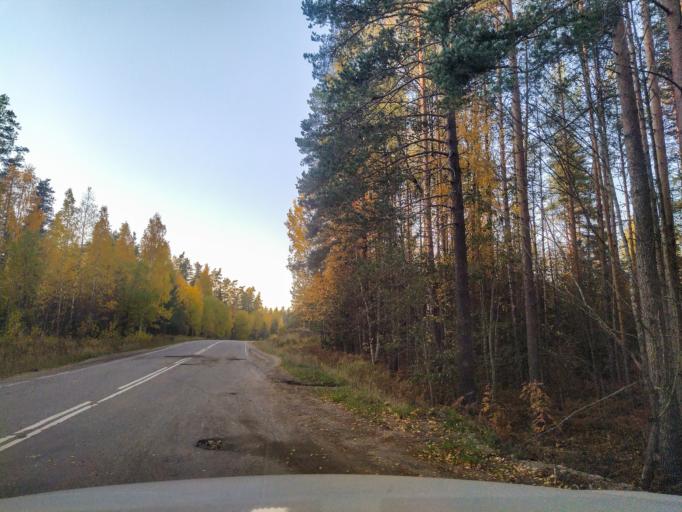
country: RU
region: Republic of Karelia
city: Lakhdenpokh'ya
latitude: 61.3809
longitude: 29.9699
